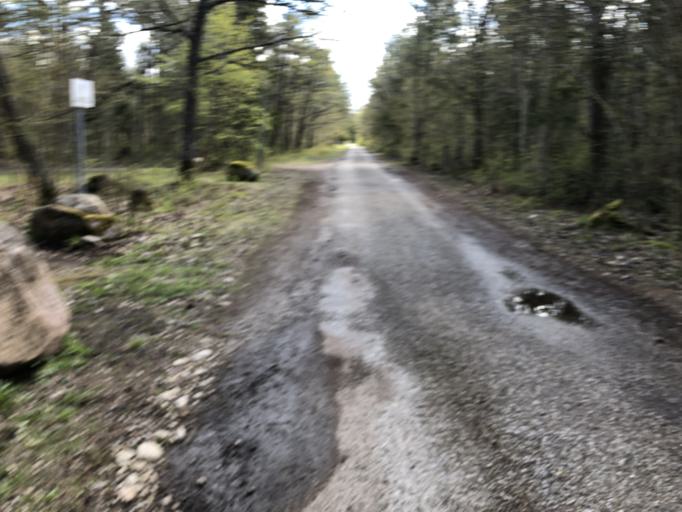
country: EE
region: Harju
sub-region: Harku vald
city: Tabasalu
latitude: 59.4376
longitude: 24.5341
